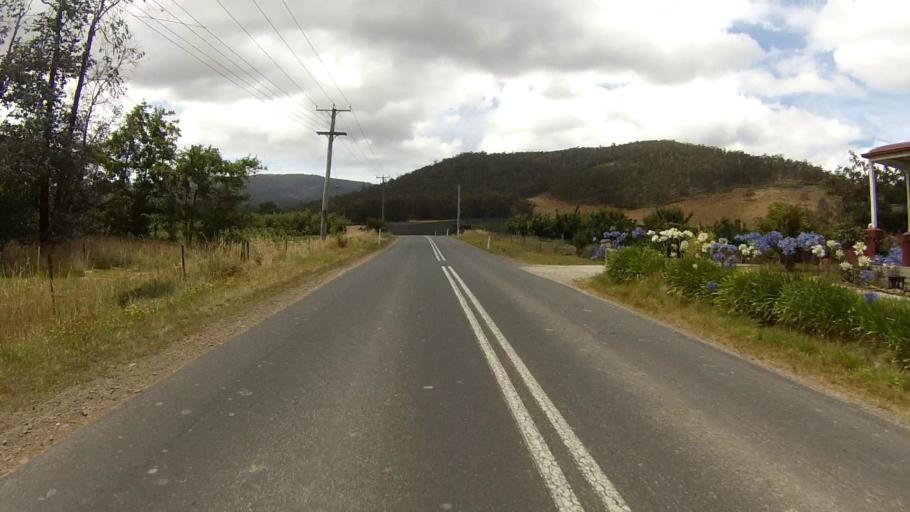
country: AU
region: Tasmania
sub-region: Huon Valley
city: Cygnet
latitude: -43.1650
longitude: 147.1310
